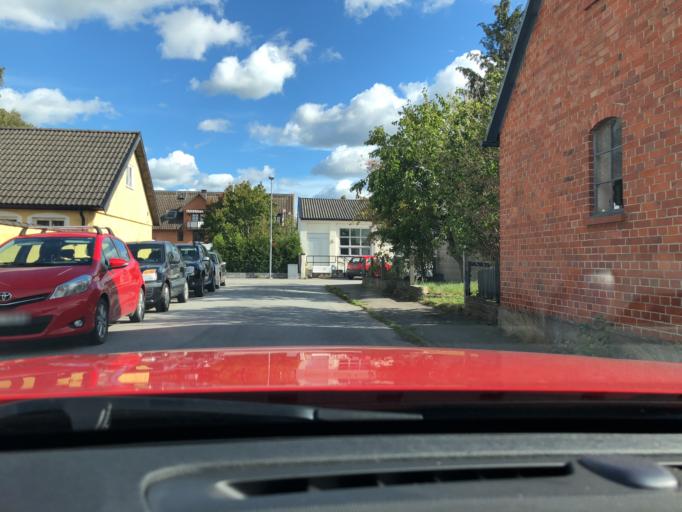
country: SE
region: Skane
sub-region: Sjobo Kommun
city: Sjoebo
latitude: 55.6336
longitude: 13.7048
